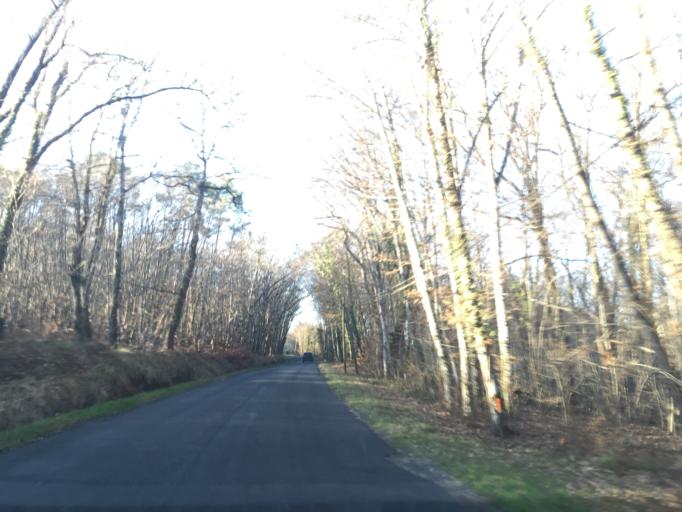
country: FR
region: Aquitaine
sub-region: Departement de la Dordogne
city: Neuvic
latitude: 45.1356
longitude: 0.4892
